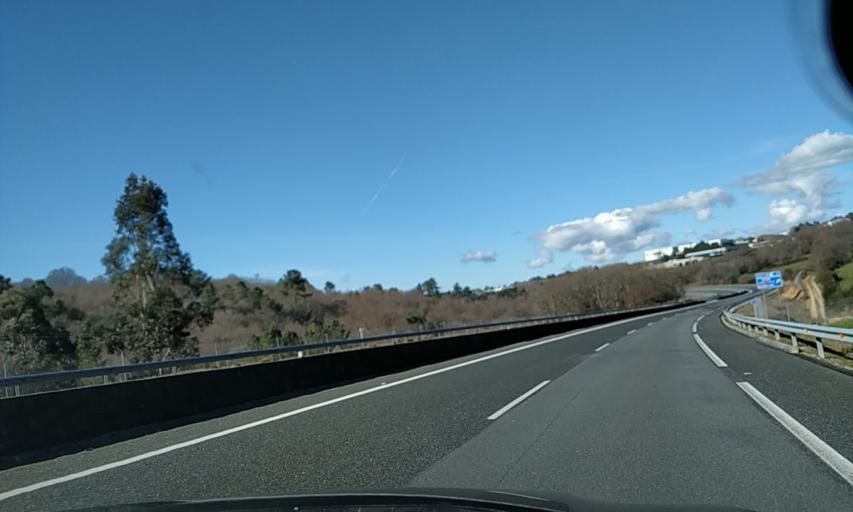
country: ES
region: Galicia
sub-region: Provincia de Pontevedra
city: Lalin
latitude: 42.6637
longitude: -8.1467
